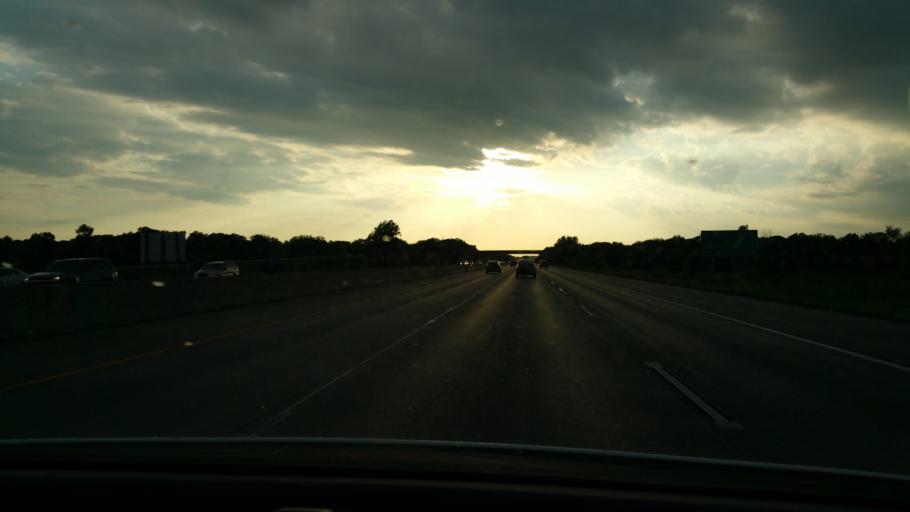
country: US
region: Iowa
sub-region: Polk County
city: Saylorville
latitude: 41.6500
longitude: -93.6478
